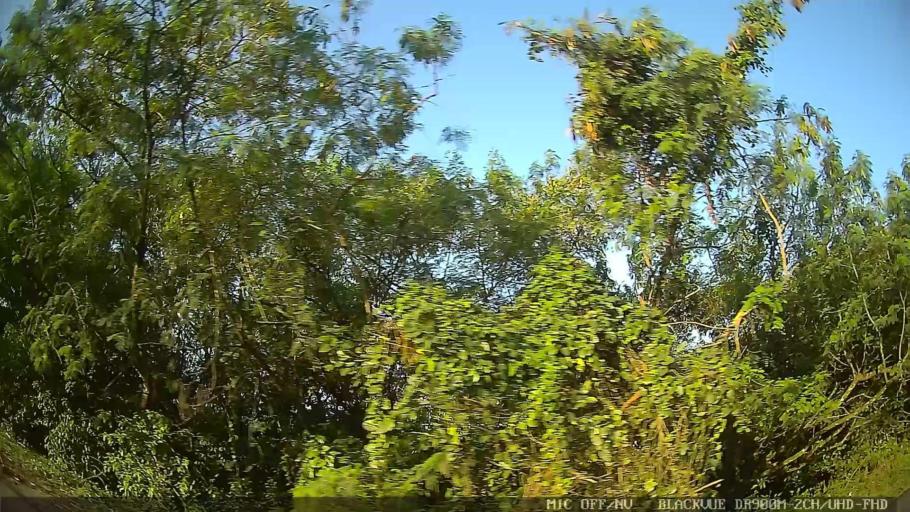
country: BR
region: Sao Paulo
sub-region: Guaruja
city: Guaruja
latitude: -23.9786
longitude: -46.2685
